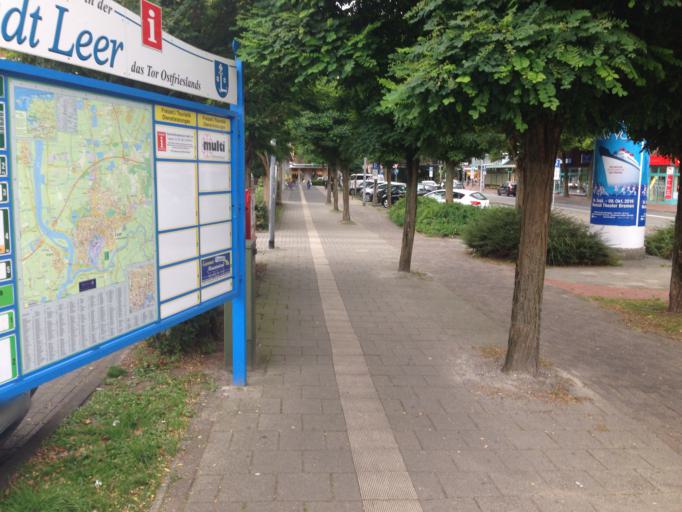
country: DE
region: Lower Saxony
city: Leer
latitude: 53.2314
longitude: 7.4640
